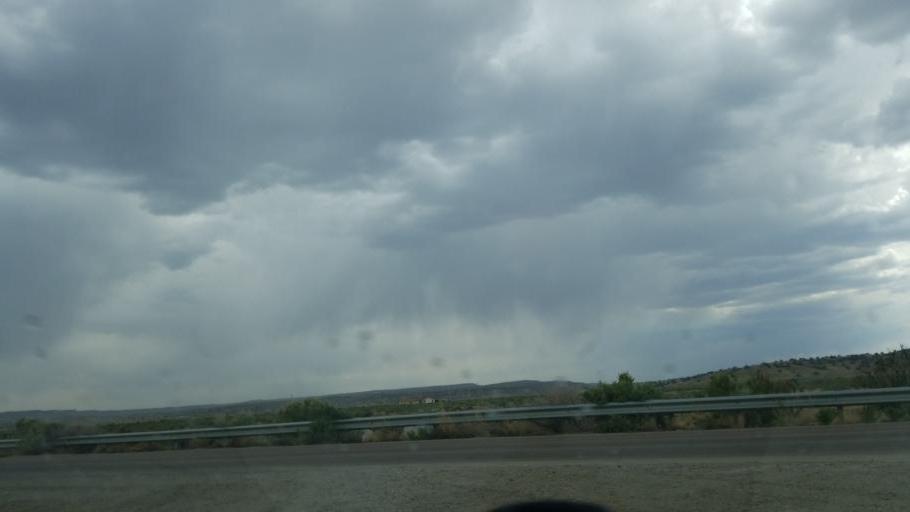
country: US
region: New Mexico
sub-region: McKinley County
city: Gallup
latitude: 35.4961
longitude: -108.9124
